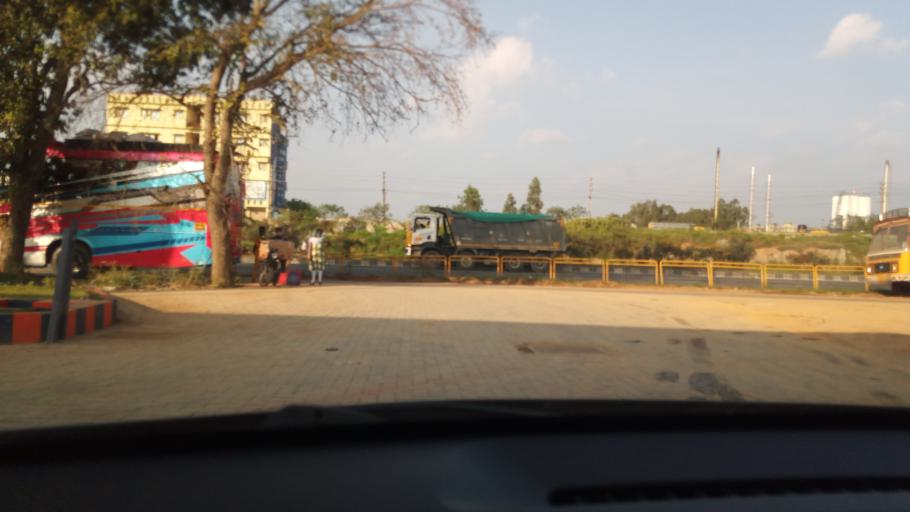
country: IN
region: Karnataka
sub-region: Bangalore Urban
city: Anekal
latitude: 12.7845
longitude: 77.7522
